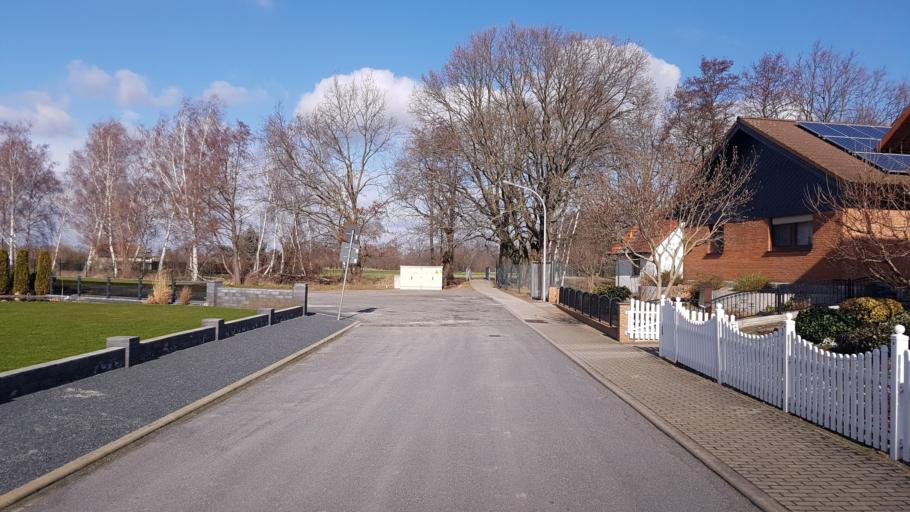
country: DE
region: Brandenburg
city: Herzberg
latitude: 51.7014
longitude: 13.2298
